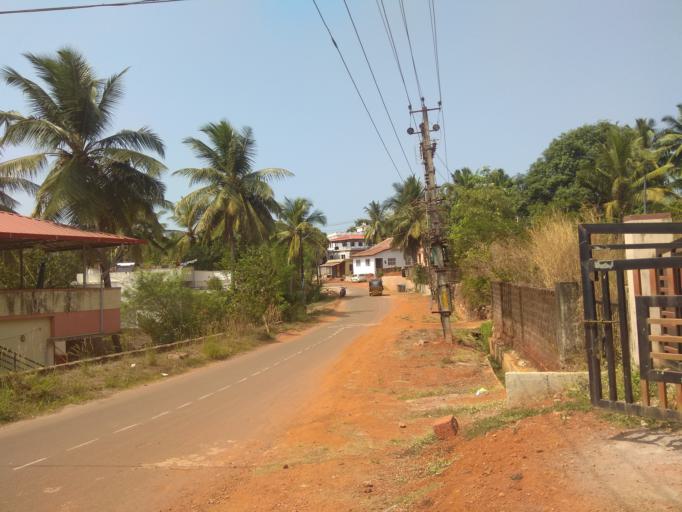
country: IN
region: Karnataka
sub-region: Dakshina Kannada
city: Mangalore
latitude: 12.9464
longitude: 74.8481
